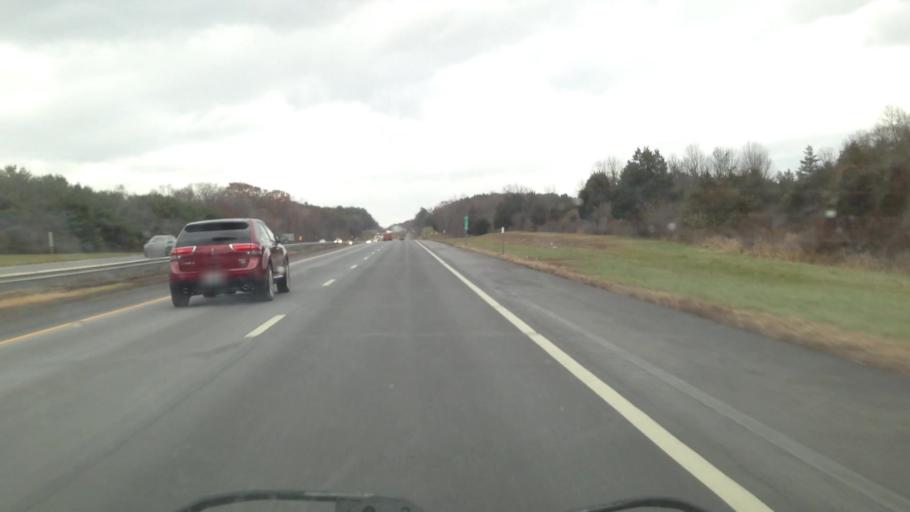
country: US
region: New York
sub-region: Greene County
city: Jefferson Heights
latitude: 42.1741
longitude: -73.9306
